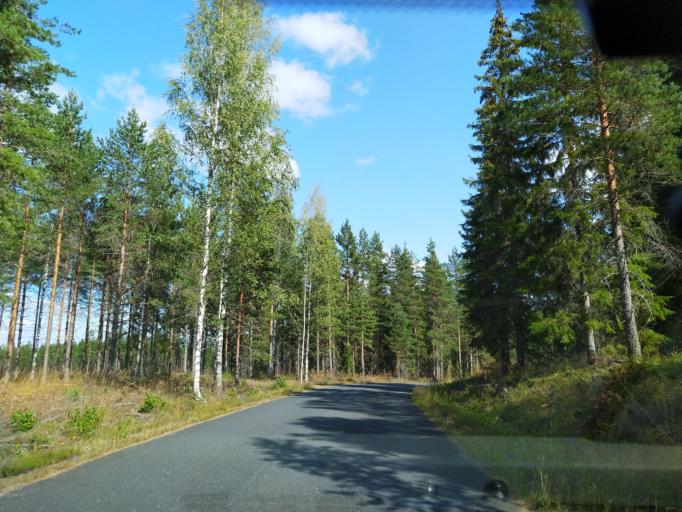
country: FI
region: Uusimaa
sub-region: Helsinki
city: Karkkila
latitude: 60.7179
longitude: 24.2000
